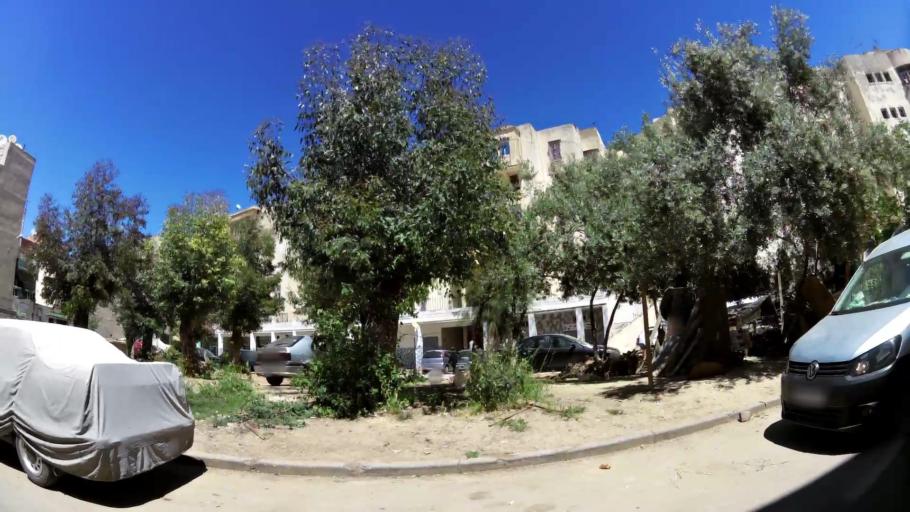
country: MA
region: Meknes-Tafilalet
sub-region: Meknes
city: Meknes
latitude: 33.9005
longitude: -5.5751
